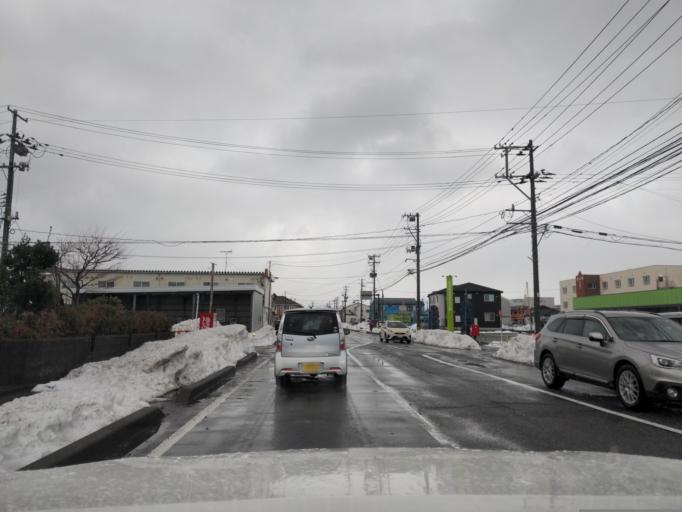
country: JP
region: Niigata
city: Kashiwazaki
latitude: 37.3590
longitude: 138.5639
